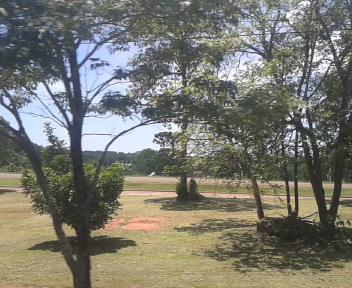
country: AR
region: Misiones
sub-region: Departamento de Leandro N. Alem
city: Leandro N. Alem
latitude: -27.6214
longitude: -55.3352
